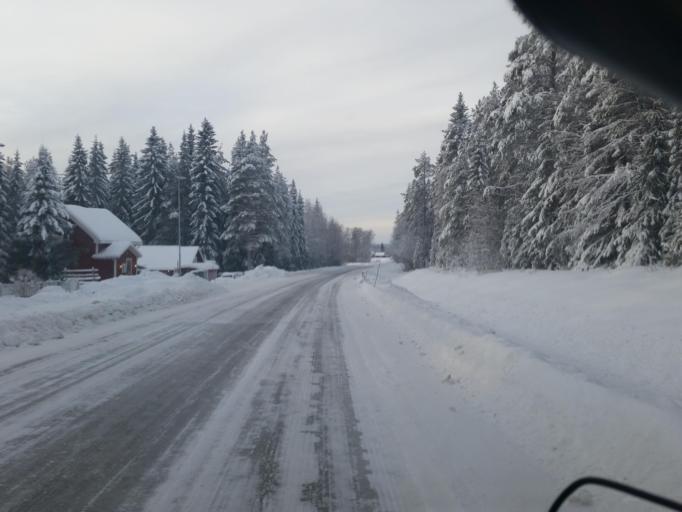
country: SE
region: Norrbotten
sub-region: Pitea Kommun
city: Norrfjarden
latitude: 65.5047
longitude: 21.3704
